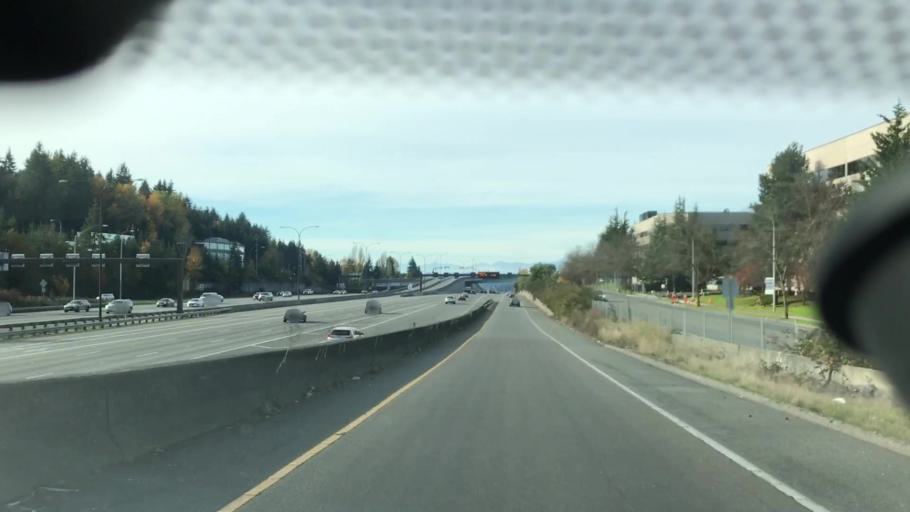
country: US
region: Washington
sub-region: King County
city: Eastgate
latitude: 47.5795
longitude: -122.1438
